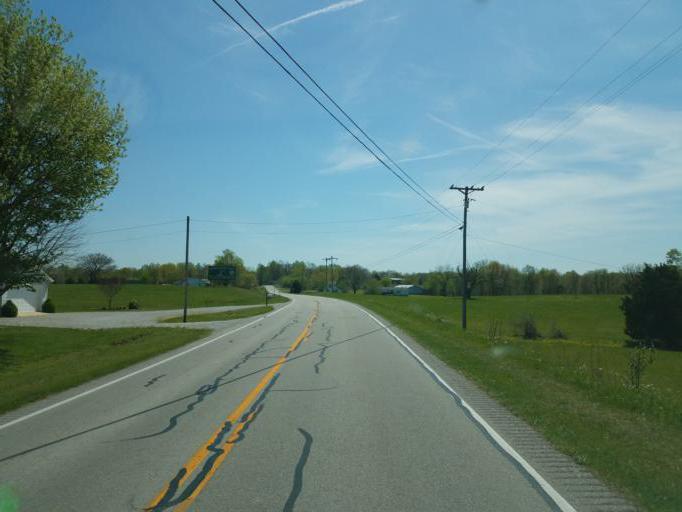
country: US
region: Kentucky
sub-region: Barren County
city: Cave City
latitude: 37.1339
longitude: -86.0356
